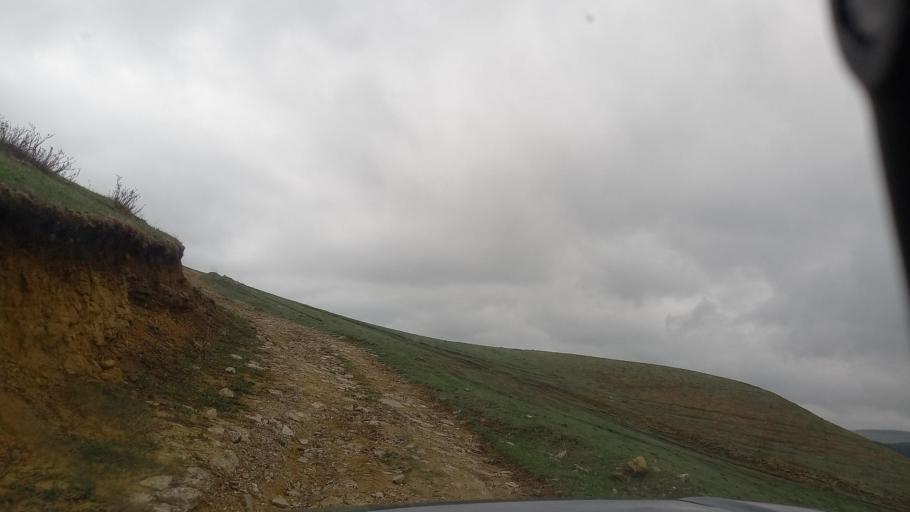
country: RU
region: Stavropol'skiy
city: Nezhinskiy
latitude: 43.8568
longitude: 42.6396
